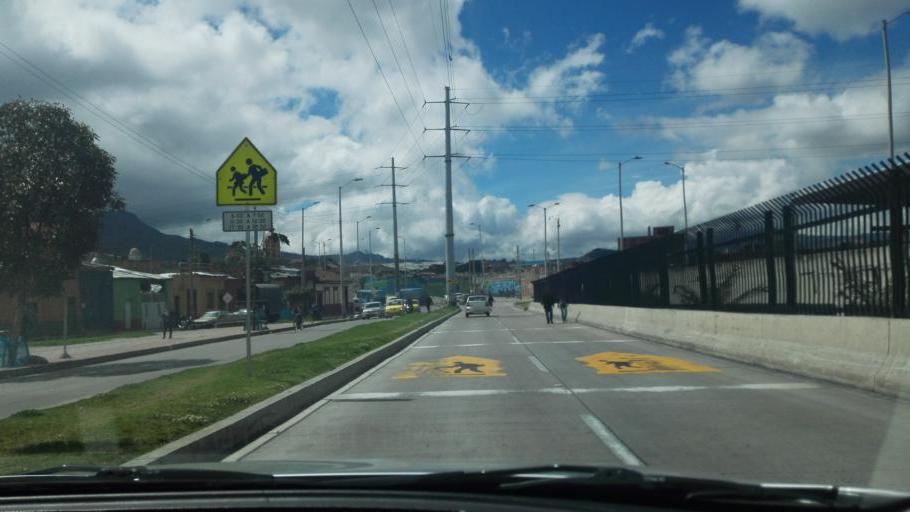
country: CO
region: Bogota D.C.
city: Bogota
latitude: 4.5935
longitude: -74.0810
